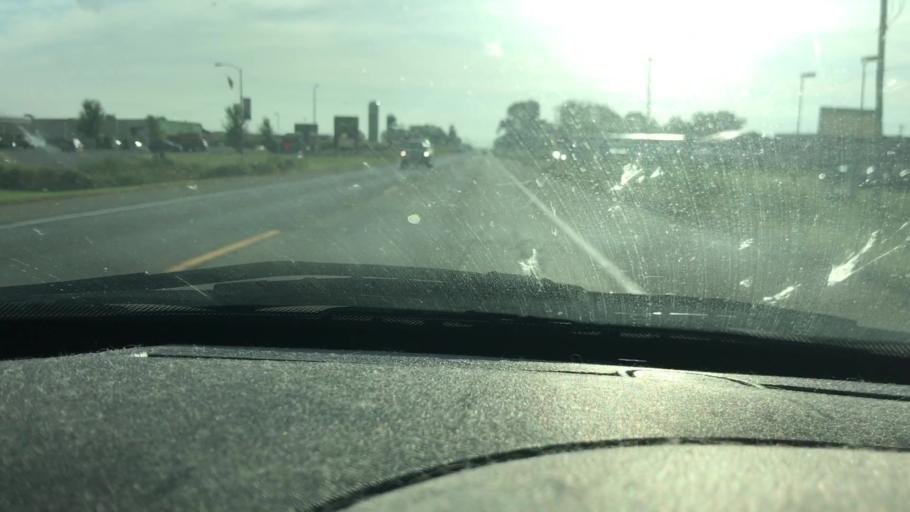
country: US
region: Wisconsin
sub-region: Outagamie County
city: Seymour
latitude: 44.5005
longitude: -88.3214
